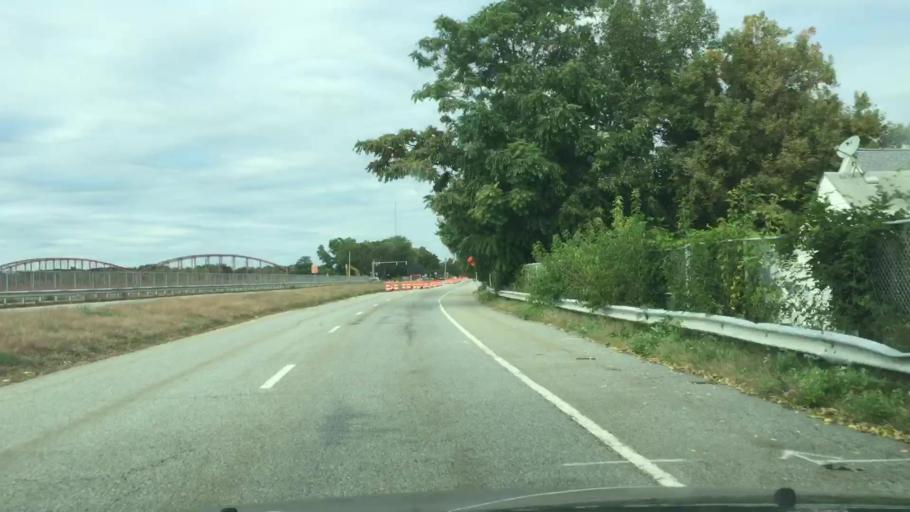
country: US
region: Massachusetts
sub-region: Middlesex County
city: Dracut
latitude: 42.6537
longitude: -71.3117
